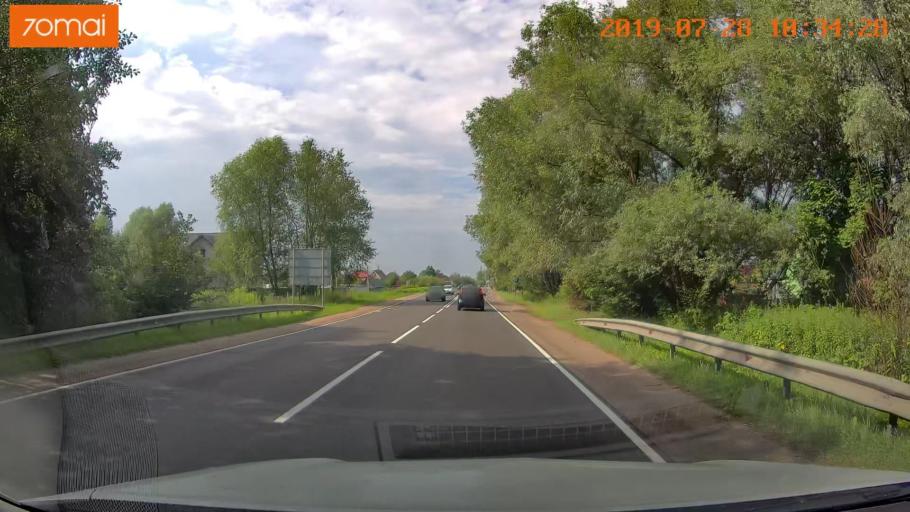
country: RU
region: Kaliningrad
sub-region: Gorod Kaliningrad
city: Kaliningrad
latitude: 54.7532
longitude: 20.4390
